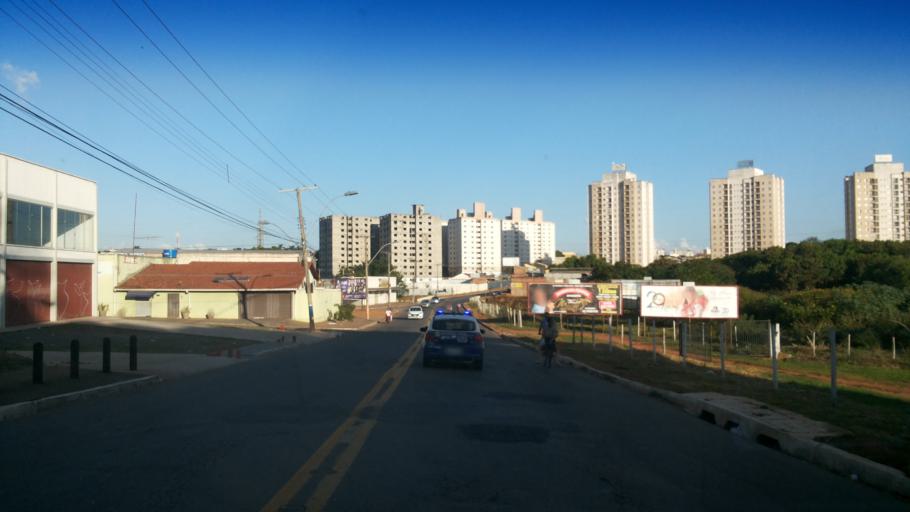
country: BR
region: Goias
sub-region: Goiania
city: Goiania
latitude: -16.6484
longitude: -49.2753
